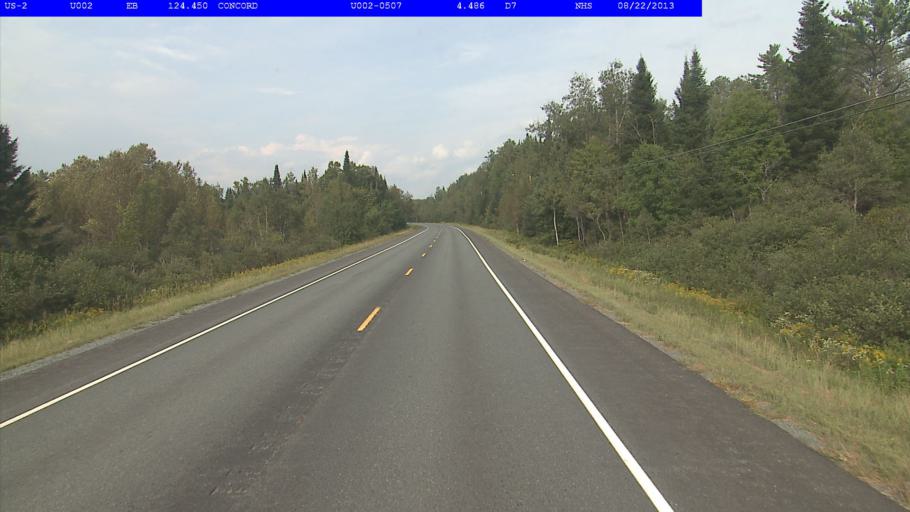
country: US
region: Vermont
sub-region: Caledonia County
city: St Johnsbury
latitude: 44.4568
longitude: -71.8668
